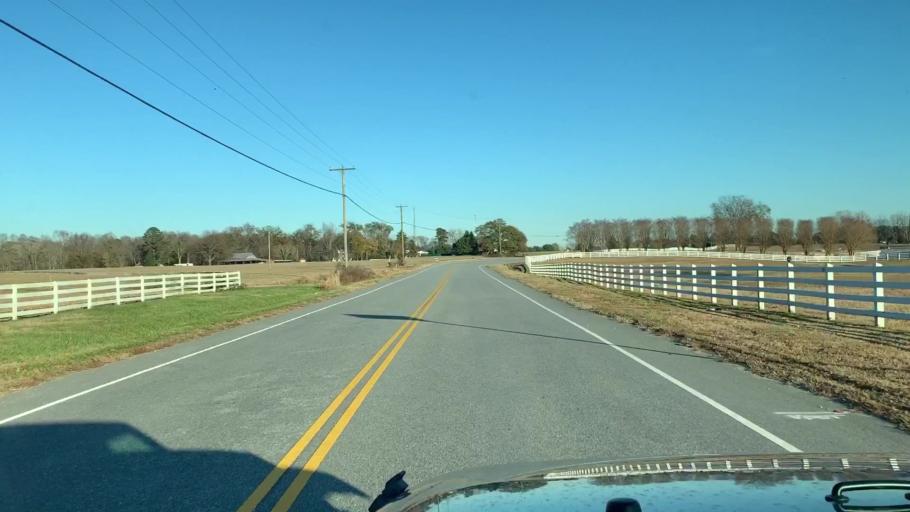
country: US
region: Virginia
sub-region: James City County
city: Williamsburg
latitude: 37.3849
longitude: -76.8186
